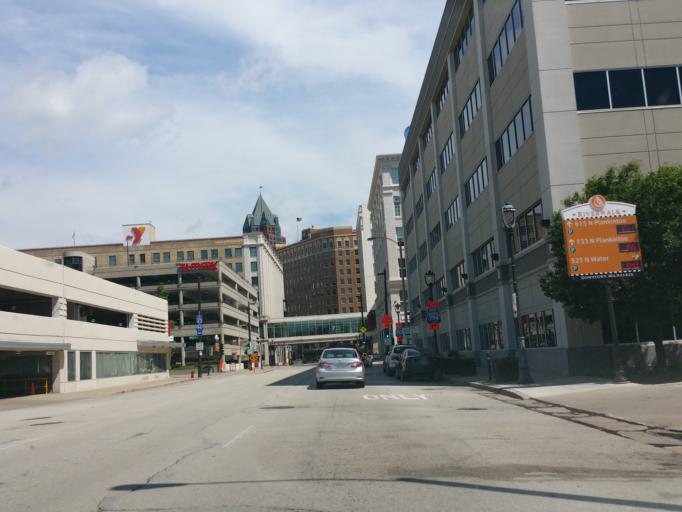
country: US
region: Wisconsin
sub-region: Milwaukee County
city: Milwaukee
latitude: 43.0367
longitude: -87.9111
